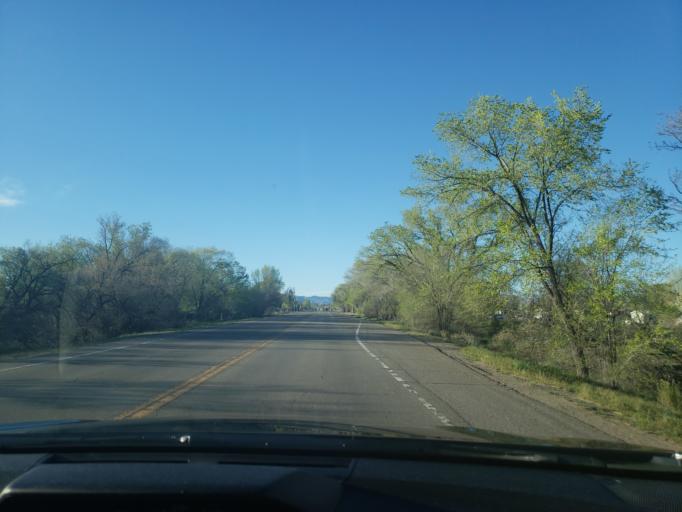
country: US
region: Colorado
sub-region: Mesa County
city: Fruita
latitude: 39.1447
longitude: -108.7382
